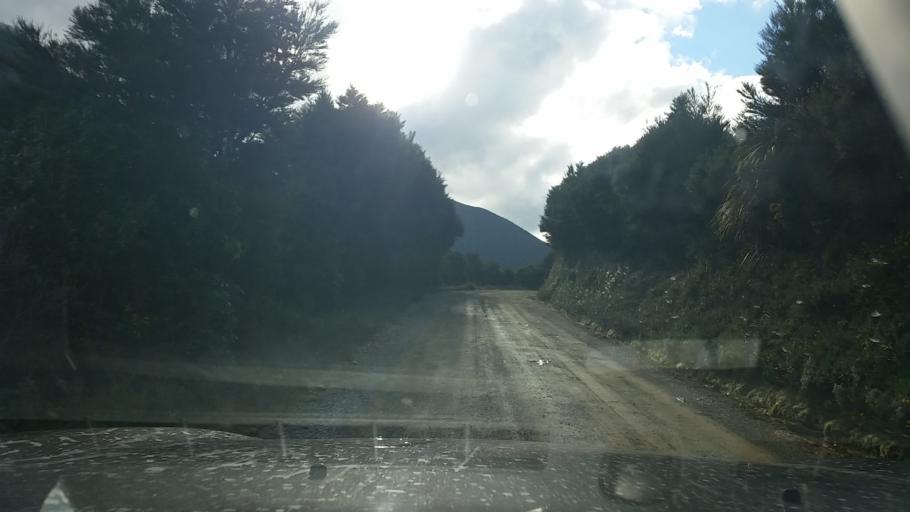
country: NZ
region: Marlborough
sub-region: Marlborough District
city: Picton
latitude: -41.1248
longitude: 174.1355
